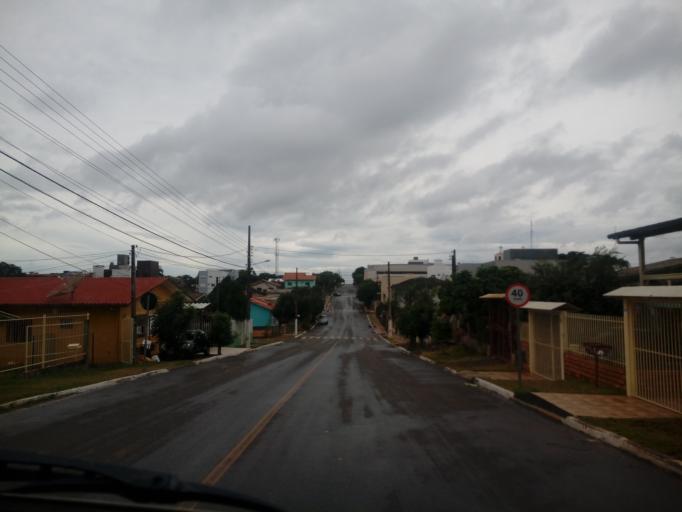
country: BR
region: Santa Catarina
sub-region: Chapeco
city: Chapeco
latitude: -27.0975
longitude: -52.6759
